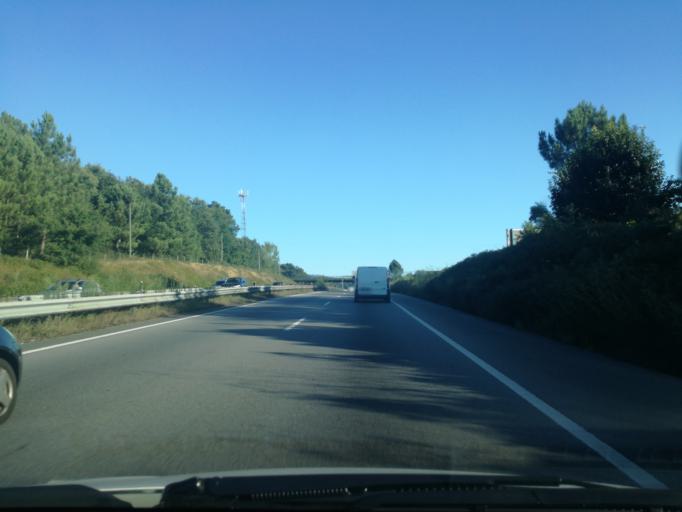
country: PT
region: Braga
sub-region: Braga
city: Adaufe
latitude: 41.5852
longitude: -8.4362
